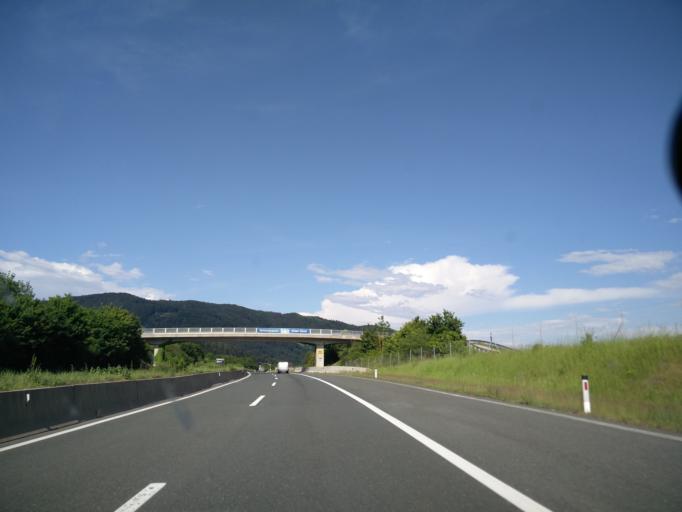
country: AT
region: Carinthia
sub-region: Politischer Bezirk Klagenfurt Land
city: Poggersdorf
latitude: 46.6509
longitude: 14.5177
